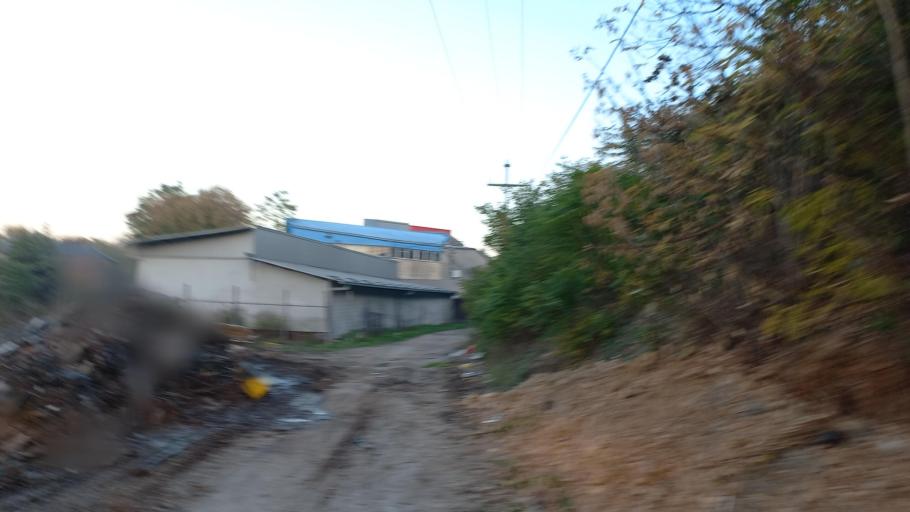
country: MK
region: Kumanovo
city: Kumanovo
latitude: 42.1420
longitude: 21.7238
